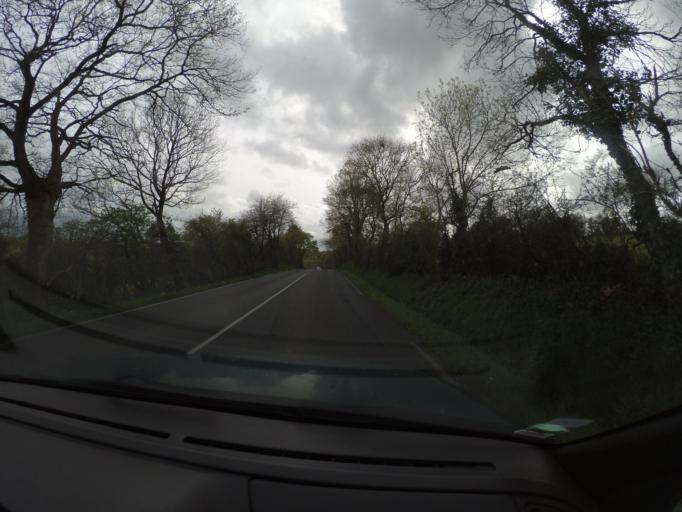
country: FR
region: Pays de la Loire
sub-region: Departement de Maine-et-Loire
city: Saint-Laurent-des-Autels
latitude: 47.3061
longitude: -1.1627
